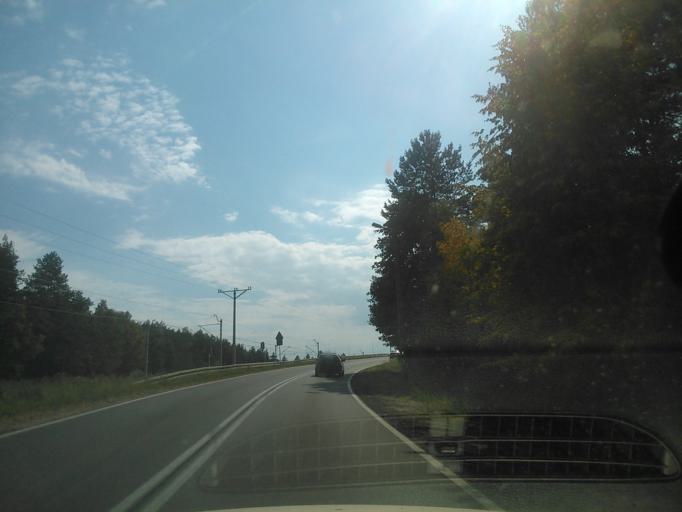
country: PL
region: Warmian-Masurian Voivodeship
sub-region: Powiat dzialdowski
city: Ilowo -Osada
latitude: 53.1453
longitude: 20.3391
